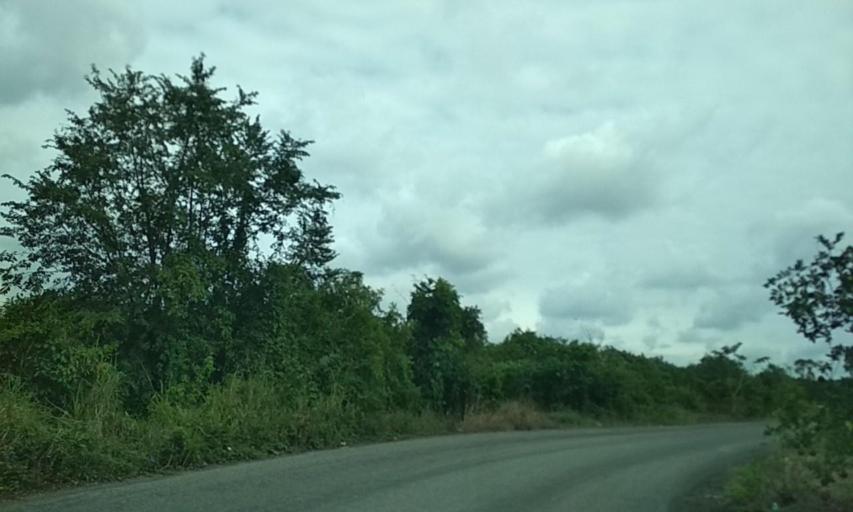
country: MX
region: Veracruz
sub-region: Papantla
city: El Chote
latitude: 20.3540
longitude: -97.3682
